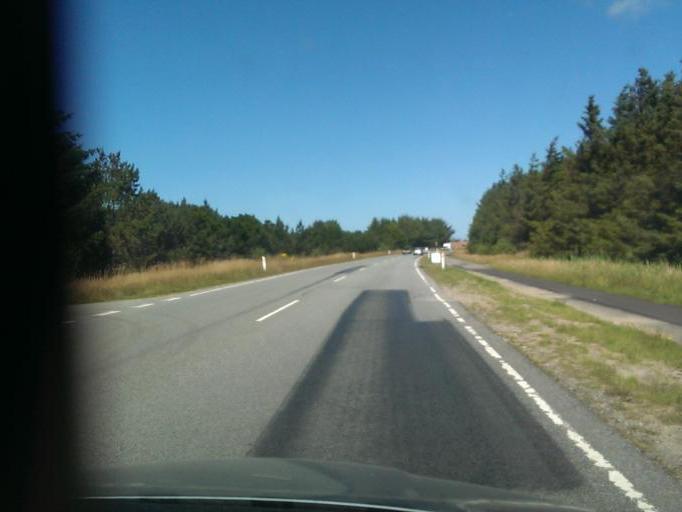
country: DK
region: North Denmark
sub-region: Jammerbugt Kommune
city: Pandrup
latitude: 57.3578
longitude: 9.7079
